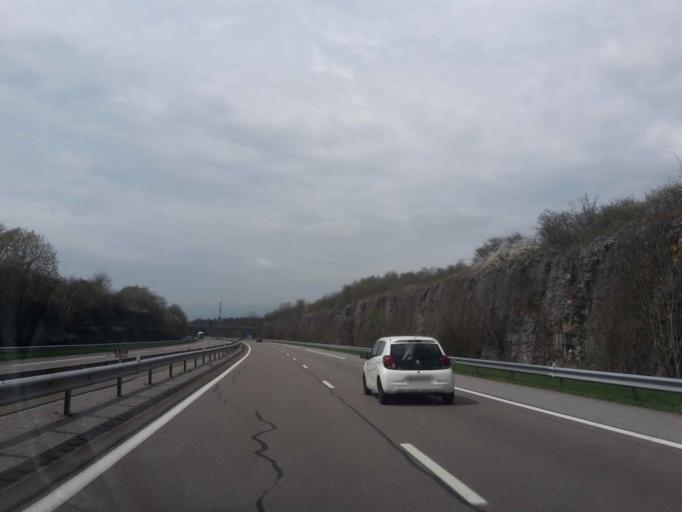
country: FR
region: Franche-Comte
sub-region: Departement du Doubs
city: Roulans
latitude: 47.3433
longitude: 6.2700
